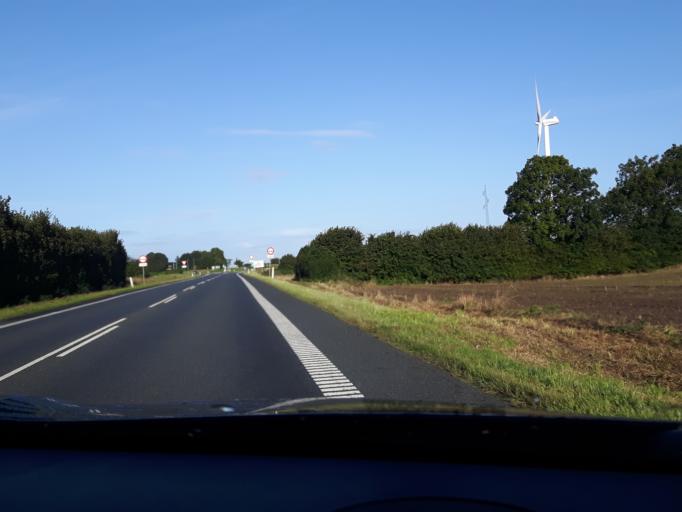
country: DK
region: South Denmark
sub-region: Middelfart Kommune
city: Ejby
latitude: 55.4549
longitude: 9.9562
